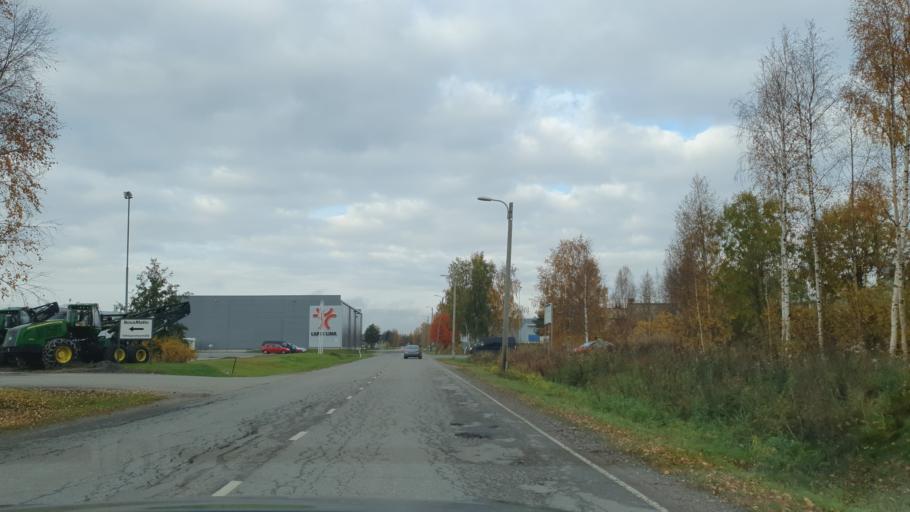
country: FI
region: Lapland
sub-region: Rovaniemi
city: Rovaniemi
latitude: 66.4929
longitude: 25.6670
